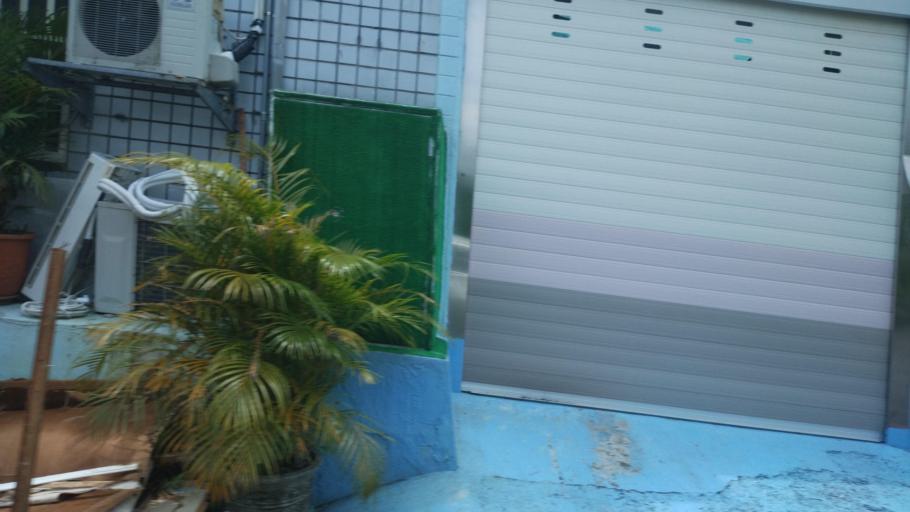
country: TW
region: Taipei
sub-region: Taipei
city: Banqiao
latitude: 24.9470
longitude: 121.4878
